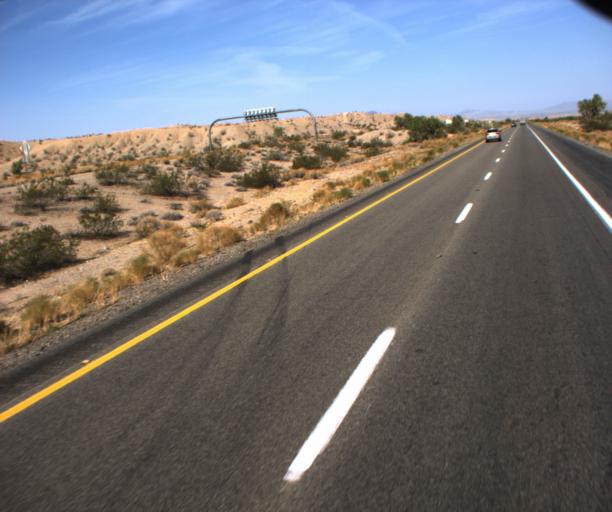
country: US
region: Arizona
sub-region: Mohave County
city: Desert Hills
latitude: 34.7287
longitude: -114.3513
